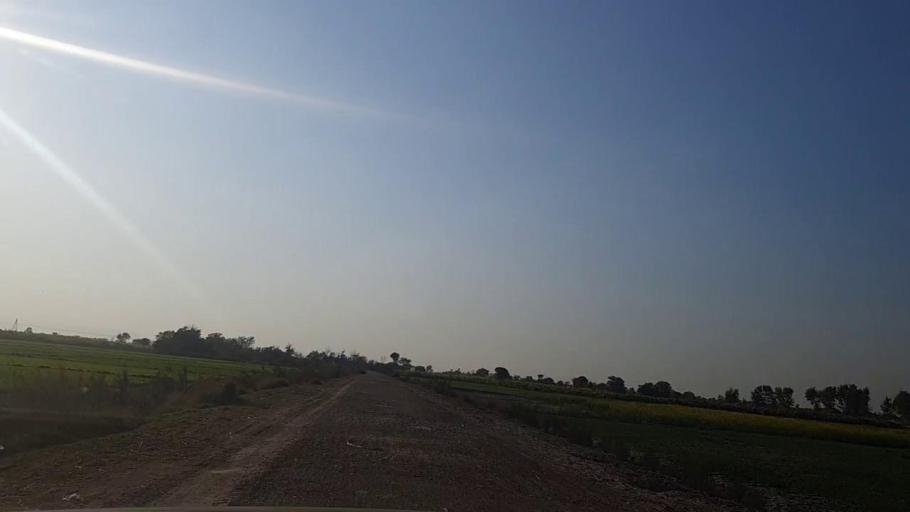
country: PK
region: Sindh
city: Sakrand
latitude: 26.3113
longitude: 68.1641
